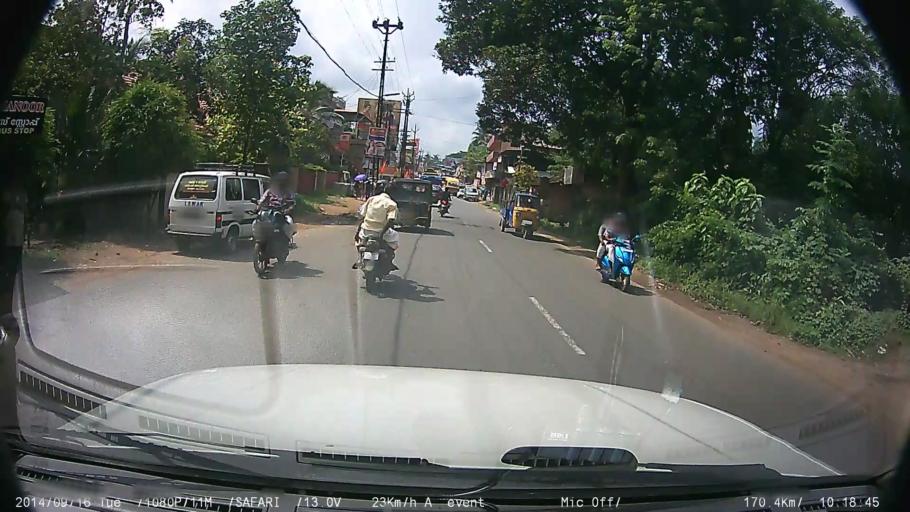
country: IN
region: Kerala
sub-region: Kottayam
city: Kottayam
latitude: 9.6750
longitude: 76.5583
